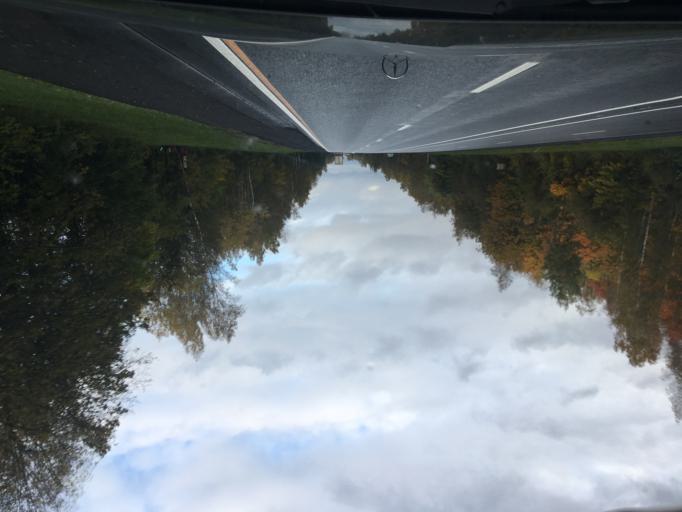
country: RU
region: Smolensk
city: Katyn'
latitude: 54.8471
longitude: 31.7519
